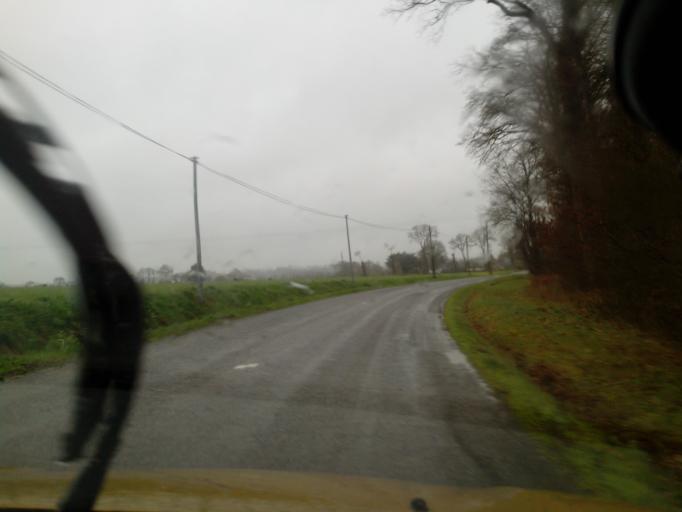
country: FR
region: Brittany
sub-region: Departement d'Ille-et-Vilaine
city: Chevaigne
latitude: 48.2306
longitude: -1.6548
